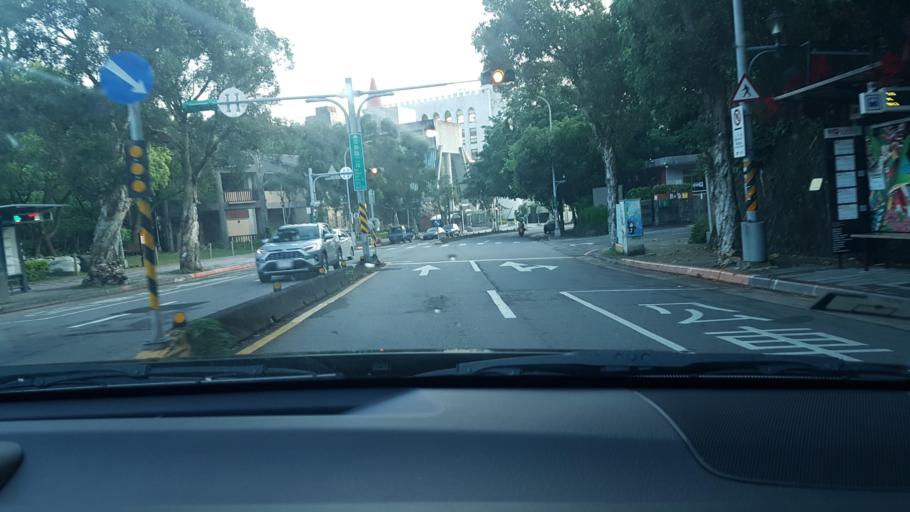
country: TW
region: Taipei
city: Taipei
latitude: 25.1021
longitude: 121.5526
